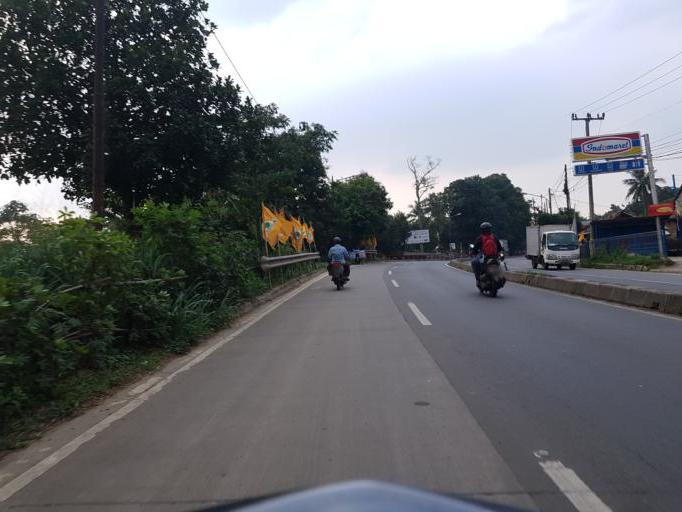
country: ID
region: West Java
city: Parung
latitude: -6.4942
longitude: 106.7480
